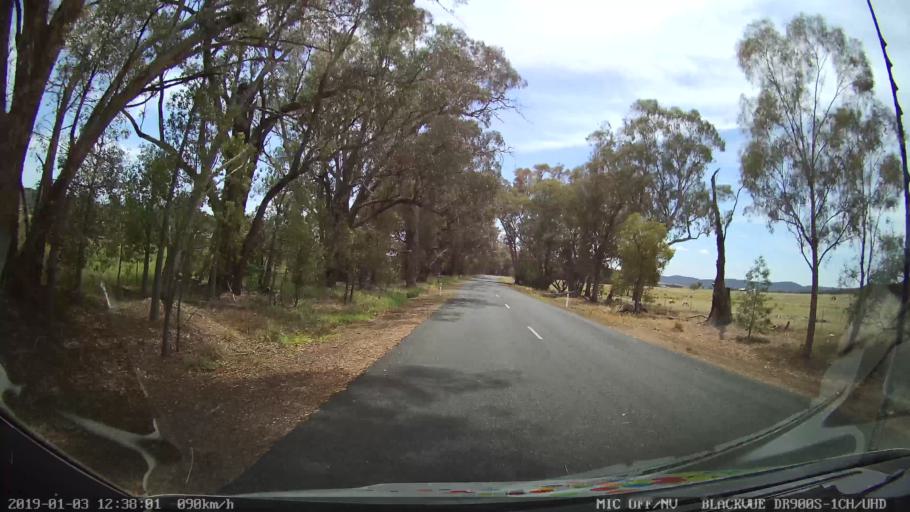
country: AU
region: New South Wales
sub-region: Weddin
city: Grenfell
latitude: -33.8373
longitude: 148.1908
